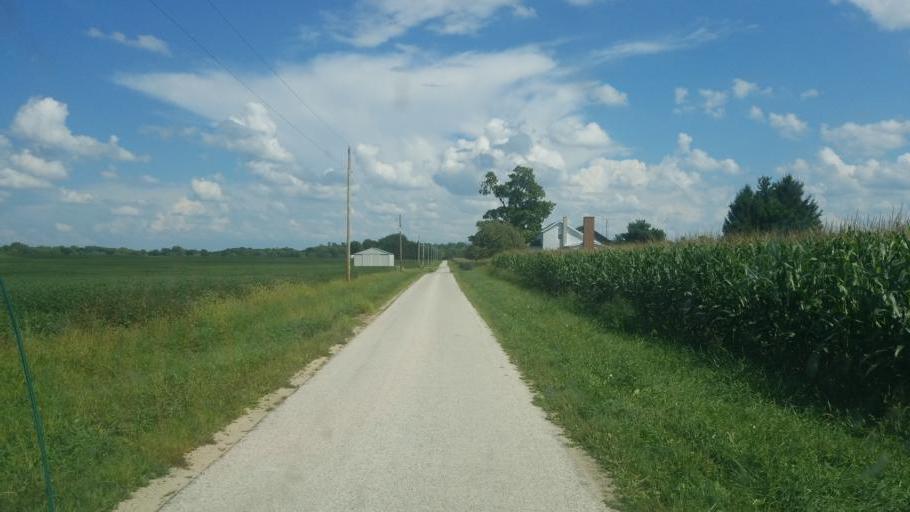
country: US
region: Ohio
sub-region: Seneca County
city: Tiffin
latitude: 40.9783
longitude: -83.2258
